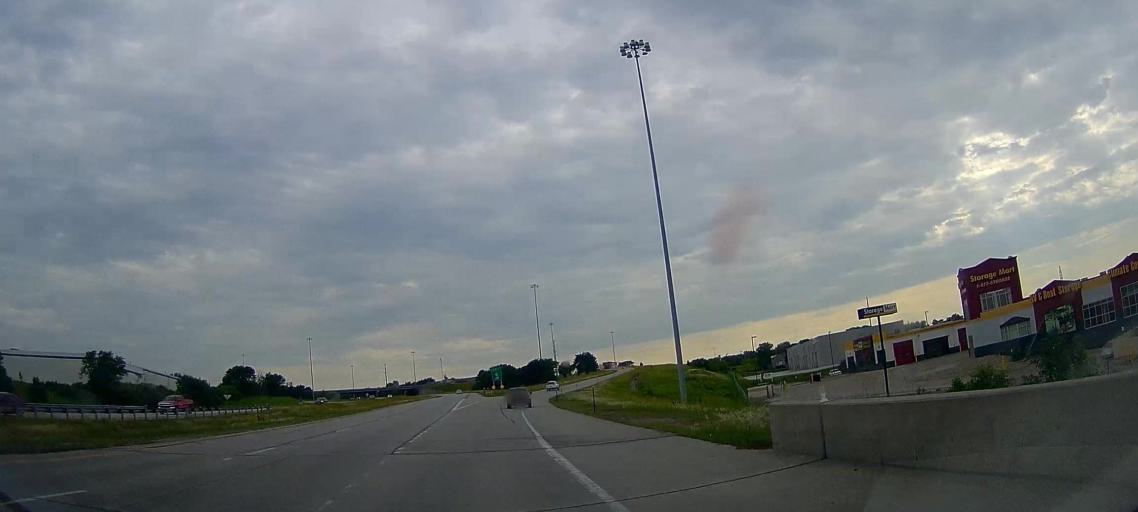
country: US
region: Nebraska
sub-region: Douglas County
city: Bennington
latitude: 41.3254
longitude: -96.0655
